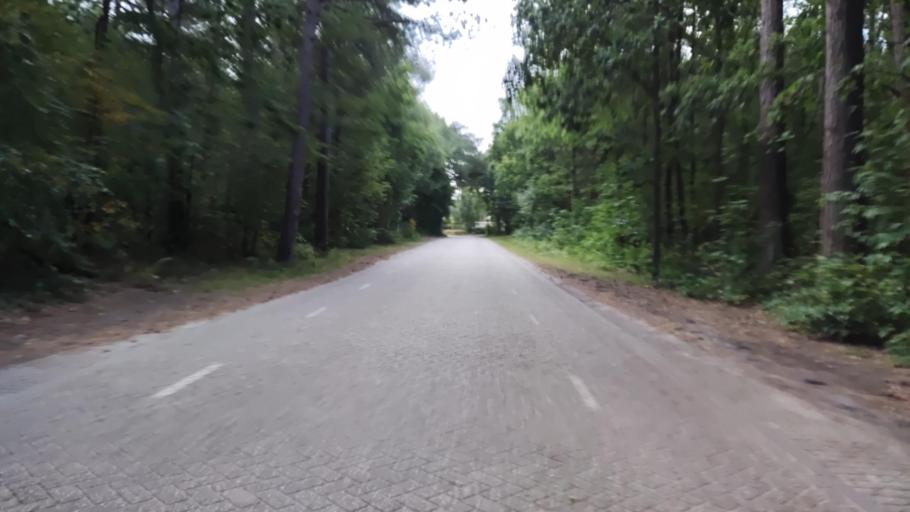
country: NL
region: North Holland
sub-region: Gemeente Texel
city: Den Burg
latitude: 53.0823
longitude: 4.7573
